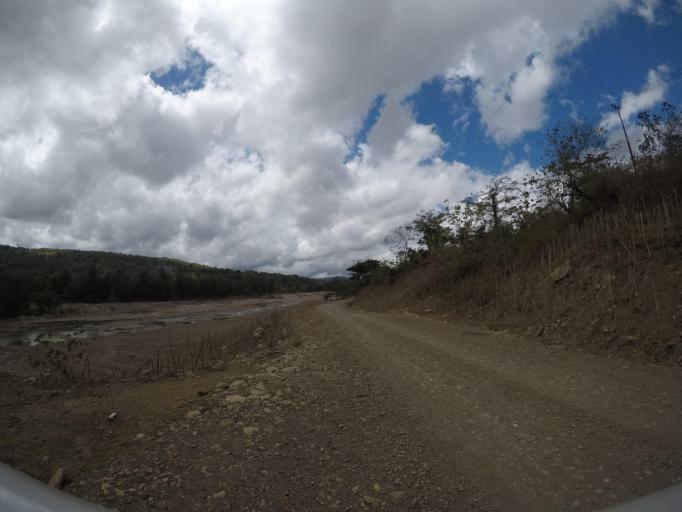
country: TL
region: Lautem
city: Lospalos
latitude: -8.5031
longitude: 126.8305
